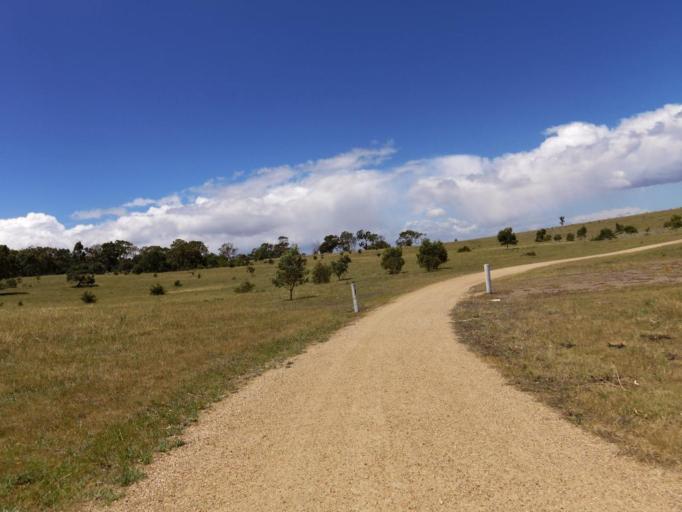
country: AU
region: Victoria
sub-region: Hume
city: Greenvale
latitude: -37.6509
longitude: 144.8469
